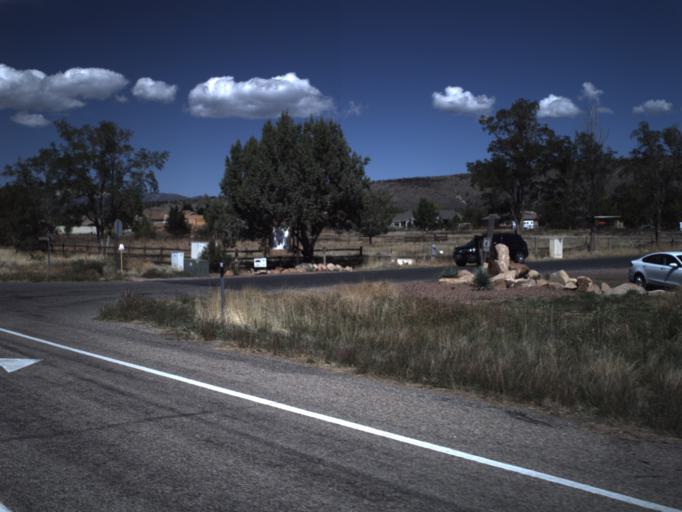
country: US
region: Utah
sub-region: Washington County
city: Ivins
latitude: 37.3050
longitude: -113.6702
